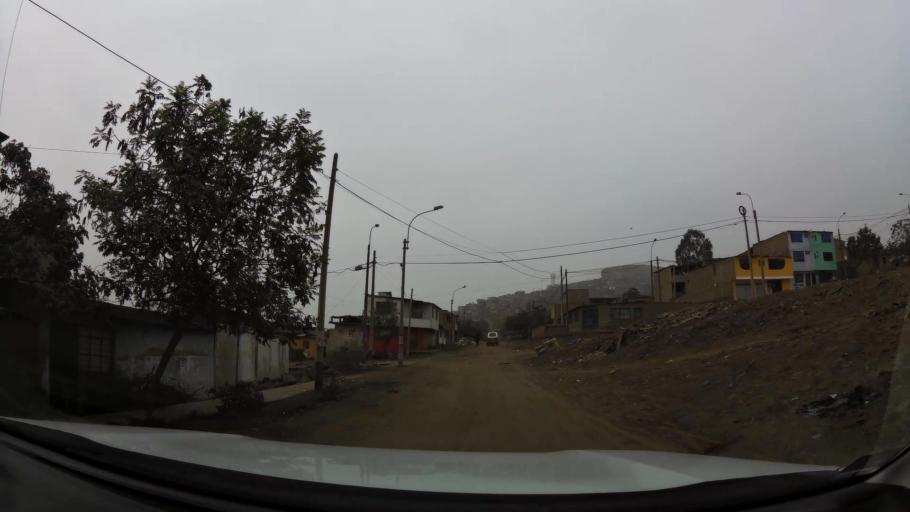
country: PE
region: Lima
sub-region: Lima
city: Surco
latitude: -12.1888
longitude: -76.9310
